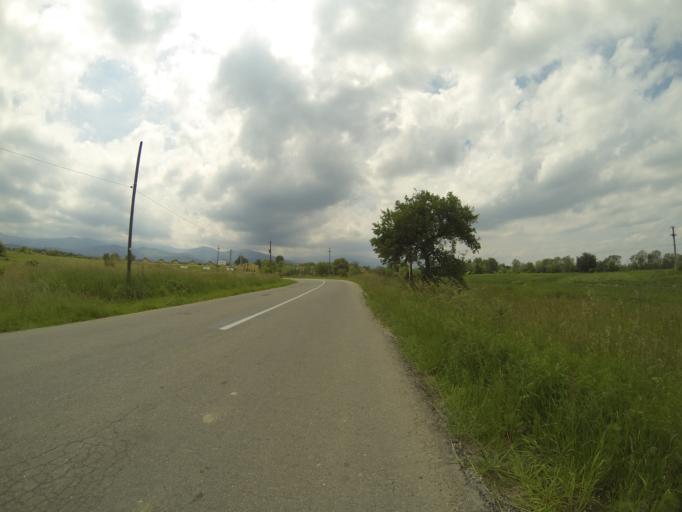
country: RO
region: Brasov
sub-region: Comuna Sinca Veche
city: Sinca Veche
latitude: 45.7507
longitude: 25.1292
